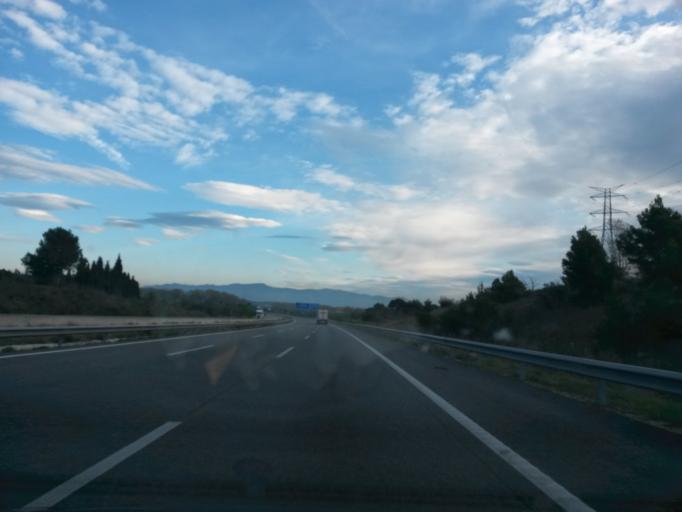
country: ES
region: Catalonia
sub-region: Provincia de Girona
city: Borrassa
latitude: 42.2117
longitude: 2.9401
